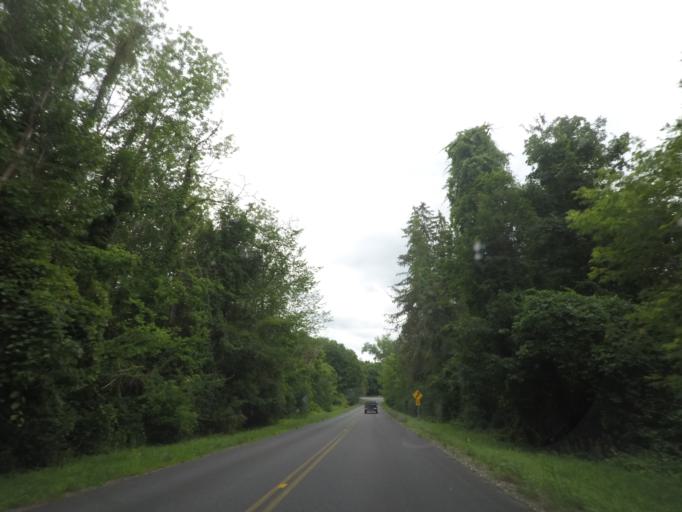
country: US
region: New York
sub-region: Saratoga County
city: Stillwater
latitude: 42.8557
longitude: -73.5486
